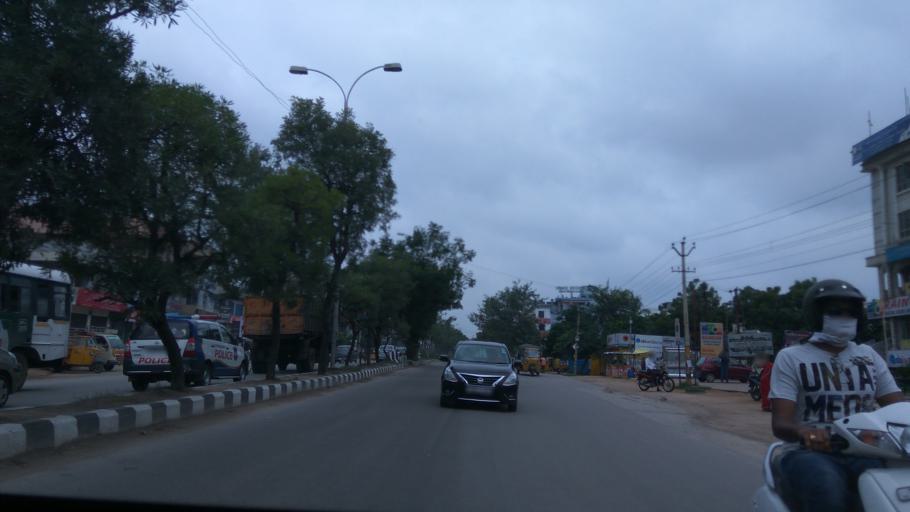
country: IN
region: Telangana
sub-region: Rangareddi
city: Secunderabad
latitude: 17.4781
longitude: 78.5615
